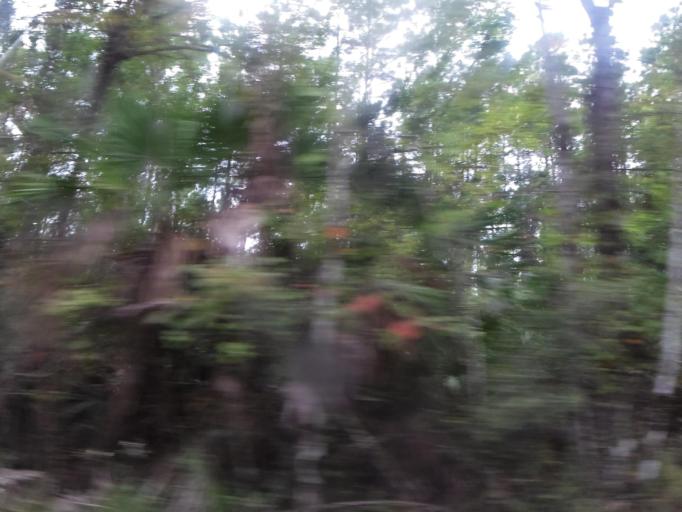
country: US
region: Florida
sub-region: Flagler County
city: Palm Coast
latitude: 29.5963
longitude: -81.3551
